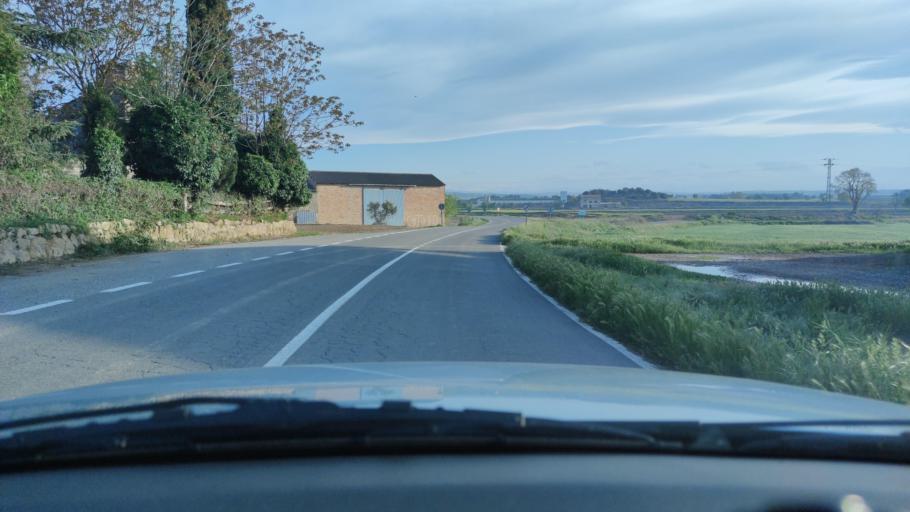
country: ES
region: Catalonia
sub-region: Provincia de Lleida
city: Agramunt
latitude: 41.7969
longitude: 1.0536
